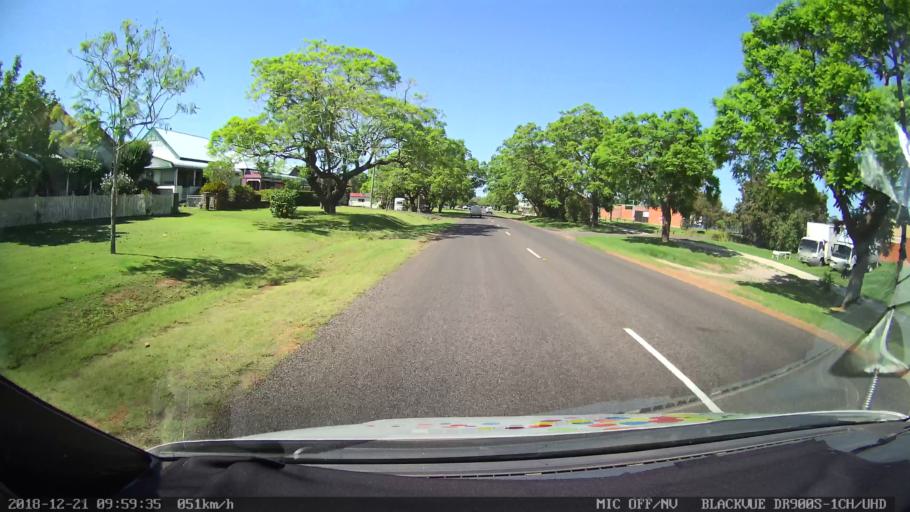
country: AU
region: New South Wales
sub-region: Clarence Valley
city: Grafton
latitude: -29.6793
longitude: 152.9297
